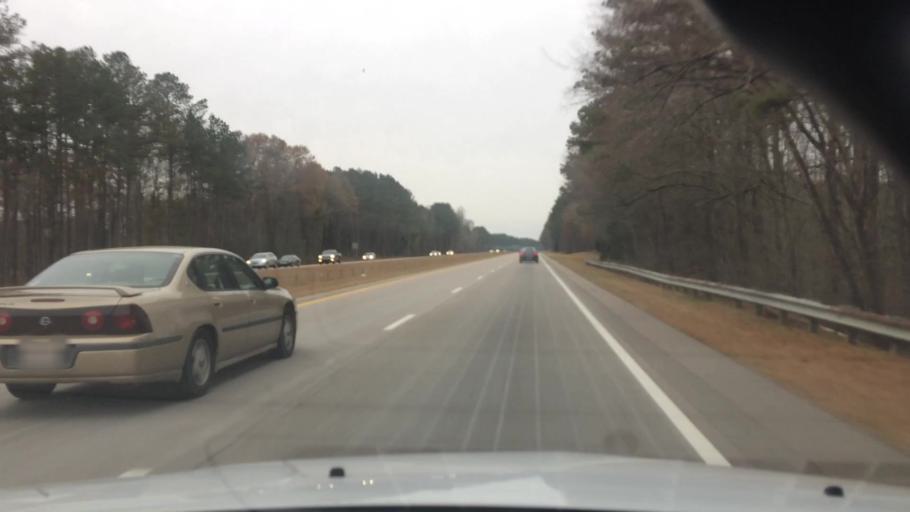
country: US
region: North Carolina
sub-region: Wake County
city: Zebulon
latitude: 35.8436
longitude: -78.2942
